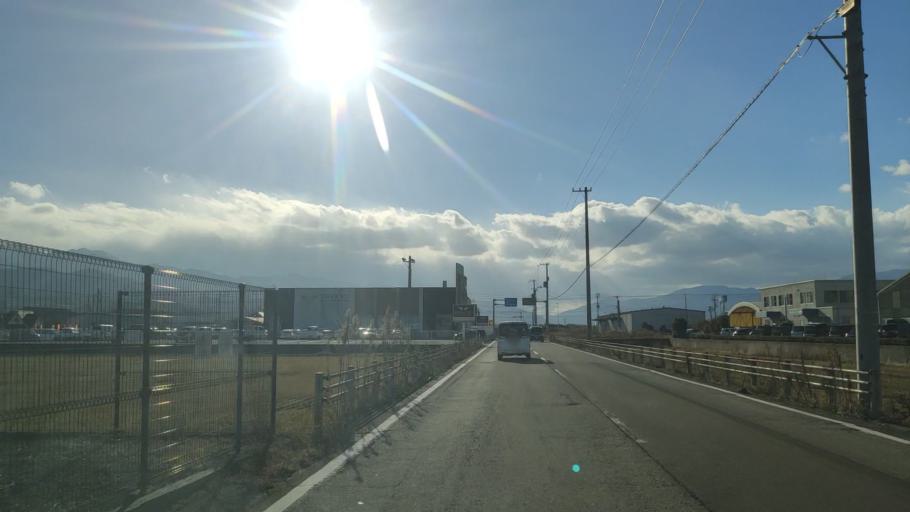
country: JP
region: Ehime
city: Saijo
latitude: 33.9116
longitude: 133.1132
